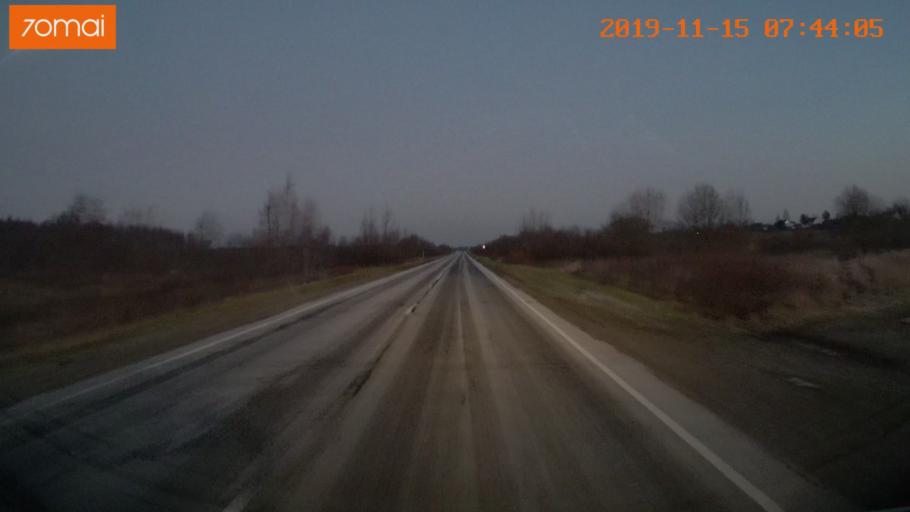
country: RU
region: Vologda
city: Sheksna
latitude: 58.8056
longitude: 38.3237
